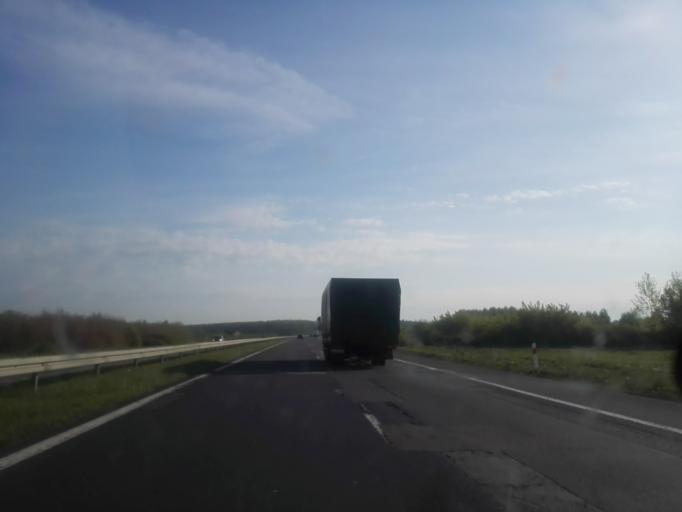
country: PL
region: Lodz Voivodeship
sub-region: Powiat piotrkowski
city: Wola Krzysztoporska
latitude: 51.2942
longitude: 19.5460
